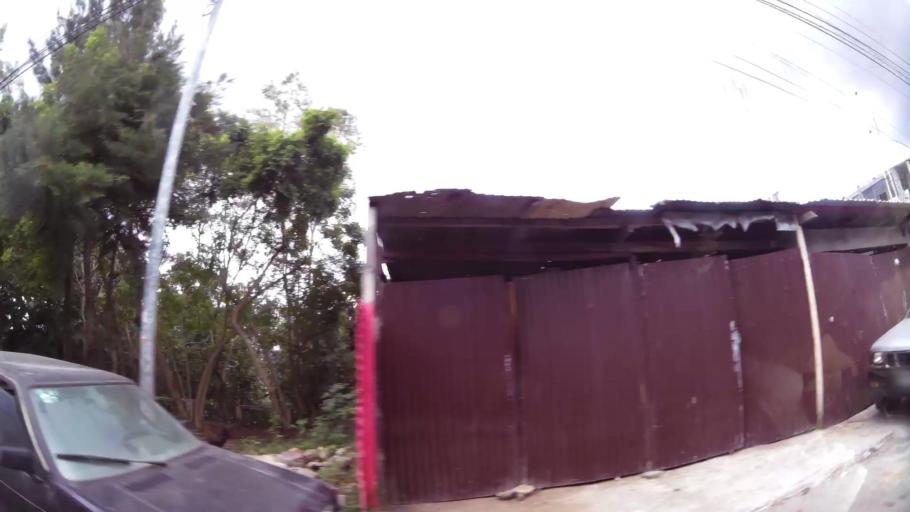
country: GT
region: Guatemala
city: Guatemala City
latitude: 14.6833
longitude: -90.5531
